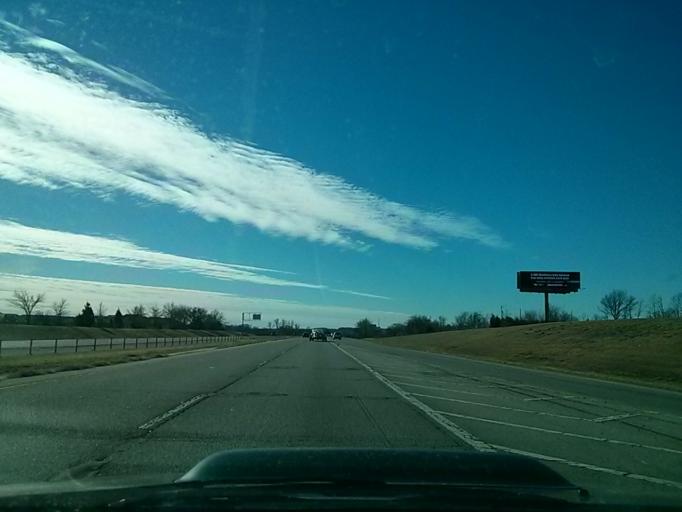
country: US
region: Oklahoma
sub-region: Tulsa County
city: Jenks
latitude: 36.0442
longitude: -96.0076
